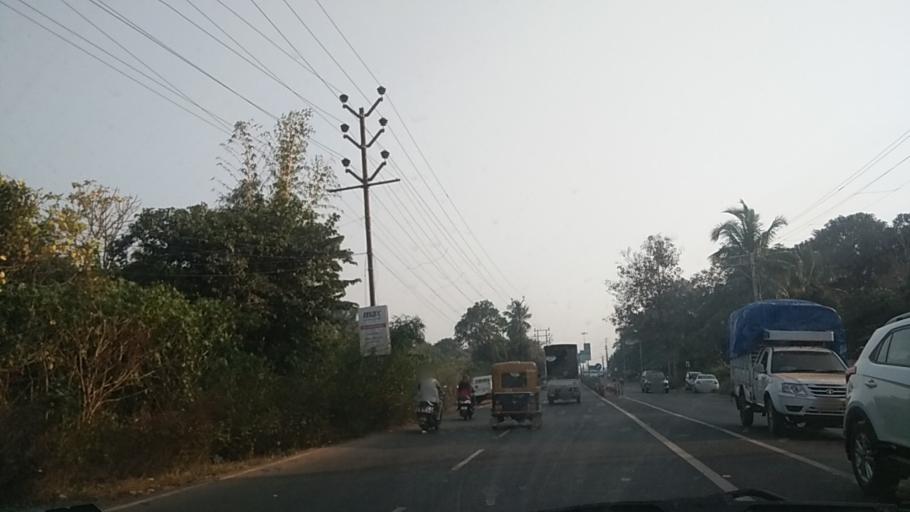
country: IN
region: Goa
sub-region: North Goa
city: Serula
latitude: 15.5338
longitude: 73.8240
